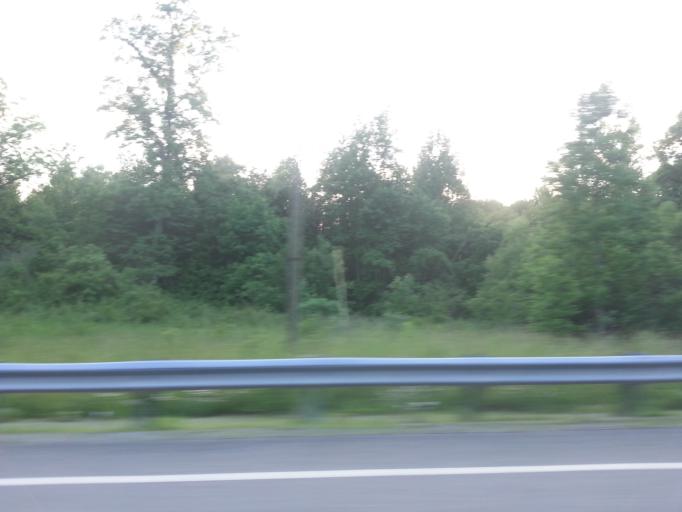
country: US
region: Tennessee
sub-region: McMinn County
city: Etowah
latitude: 35.2413
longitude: -84.3180
